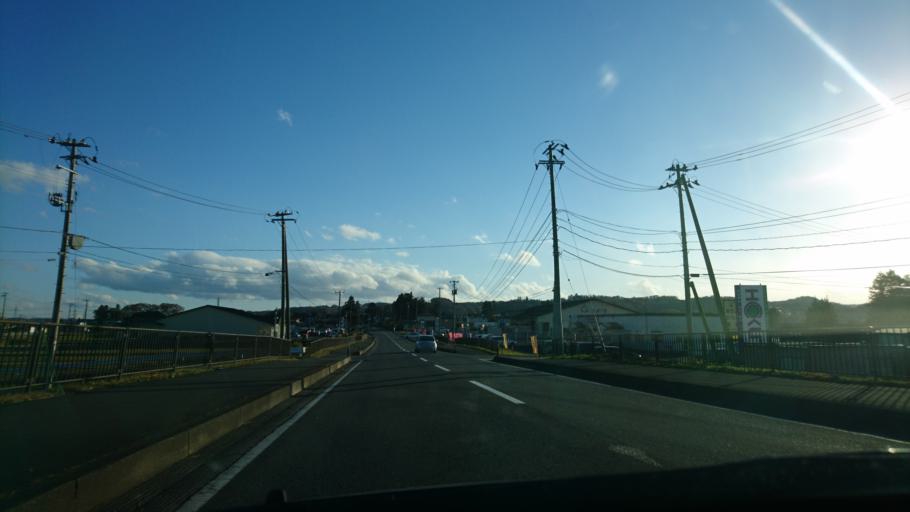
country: JP
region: Iwate
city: Ichinoseki
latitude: 38.9826
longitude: 141.1164
